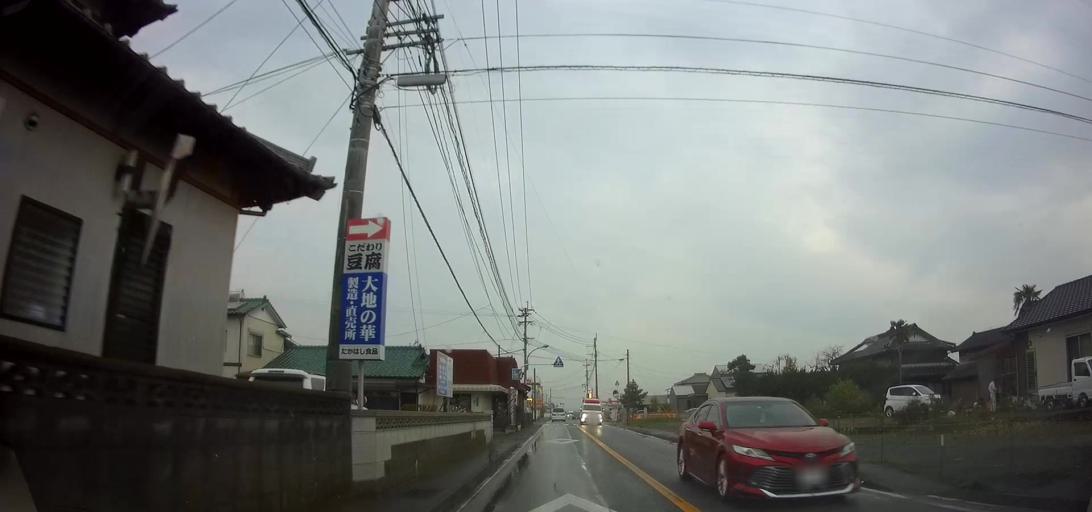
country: JP
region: Nagasaki
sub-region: Isahaya-shi
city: Isahaya
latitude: 32.8350
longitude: 130.1108
